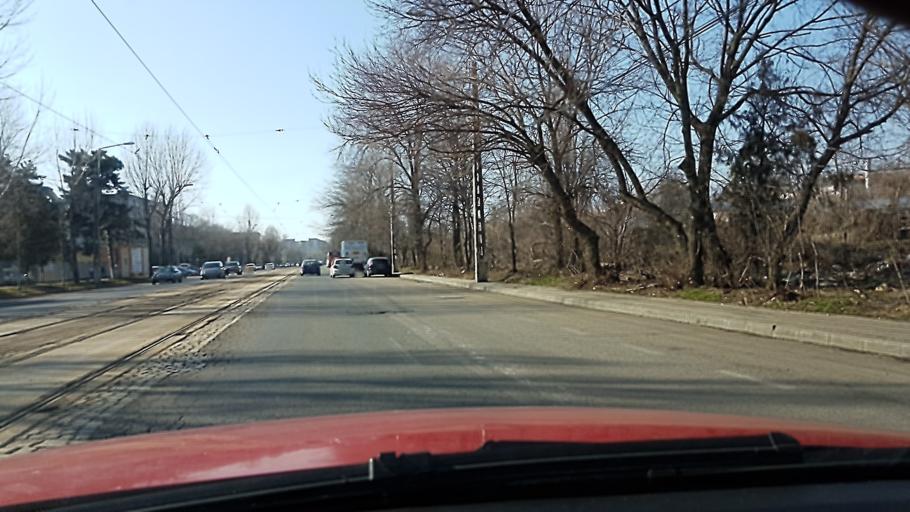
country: RO
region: Ilfov
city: Dobroesti
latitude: 44.4345
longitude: 26.1824
